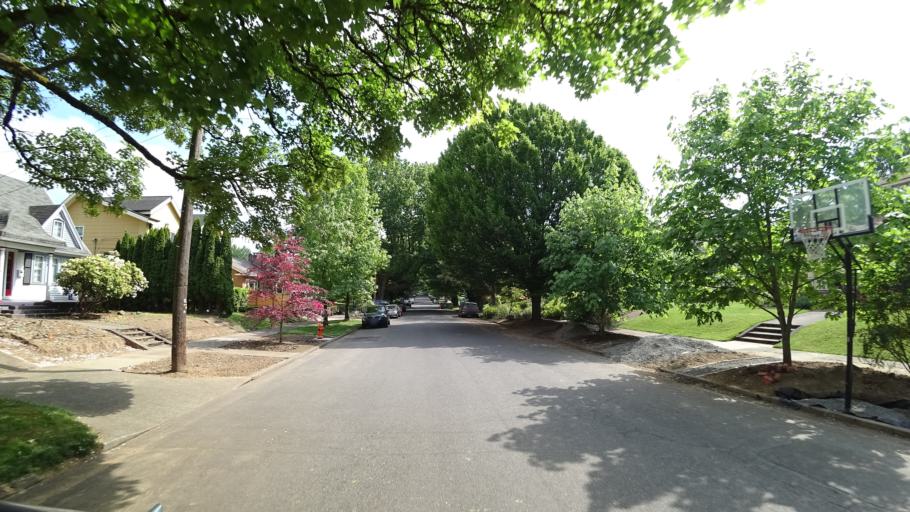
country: US
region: Oregon
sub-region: Multnomah County
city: Portland
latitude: 45.5476
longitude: -122.6483
